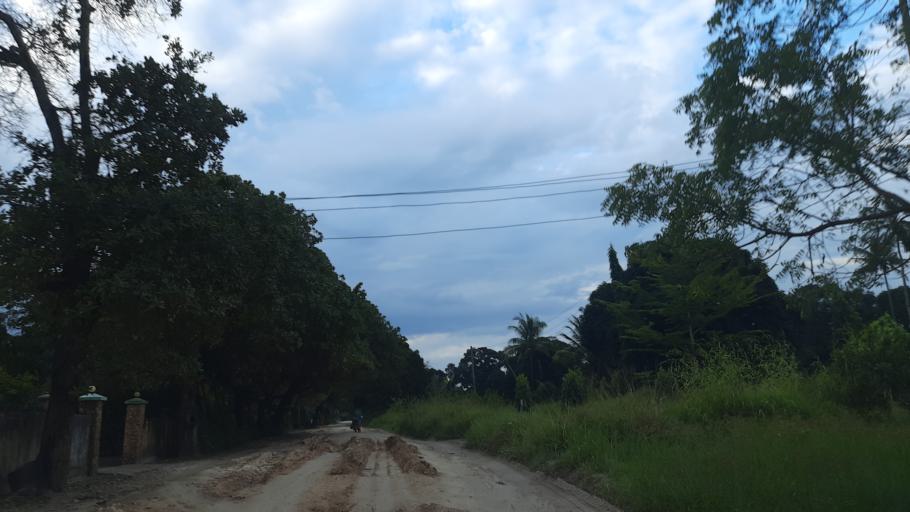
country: TZ
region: Pwani
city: Bagamoyo
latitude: -6.5168
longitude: 38.9289
